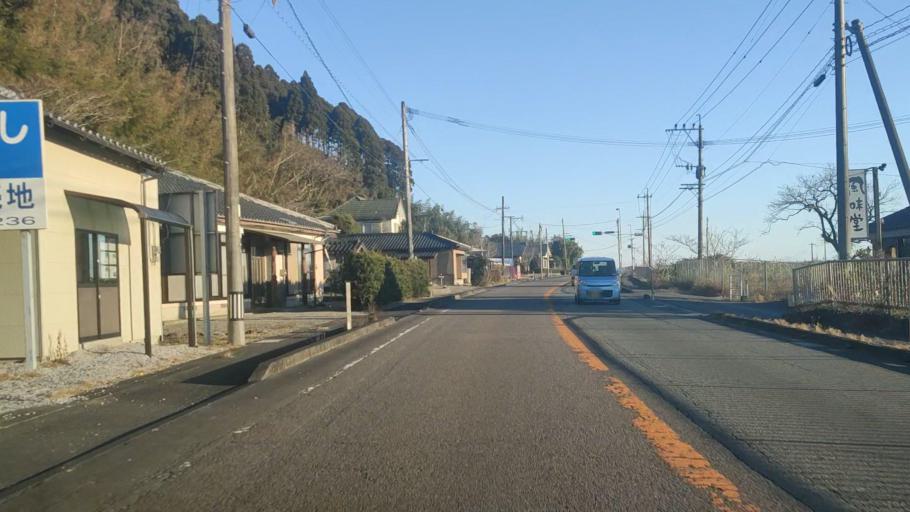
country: JP
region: Miyazaki
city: Takanabe
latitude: 32.0842
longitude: 131.5108
